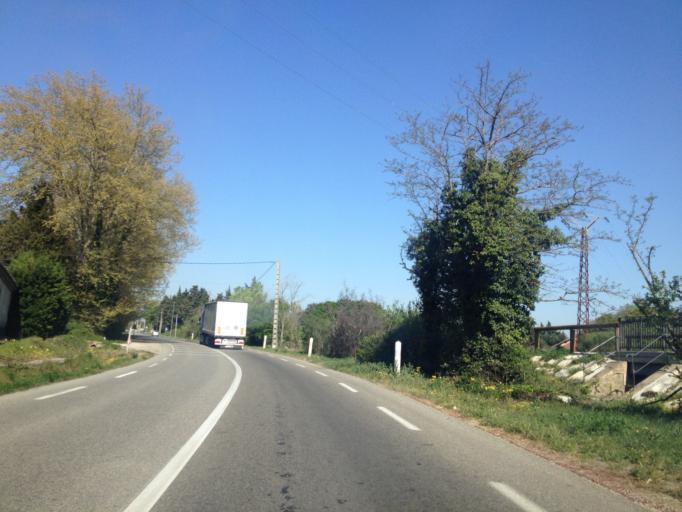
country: FR
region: Provence-Alpes-Cote d'Azur
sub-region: Departement du Vaucluse
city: Sarrians
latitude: 44.0983
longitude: 4.9449
